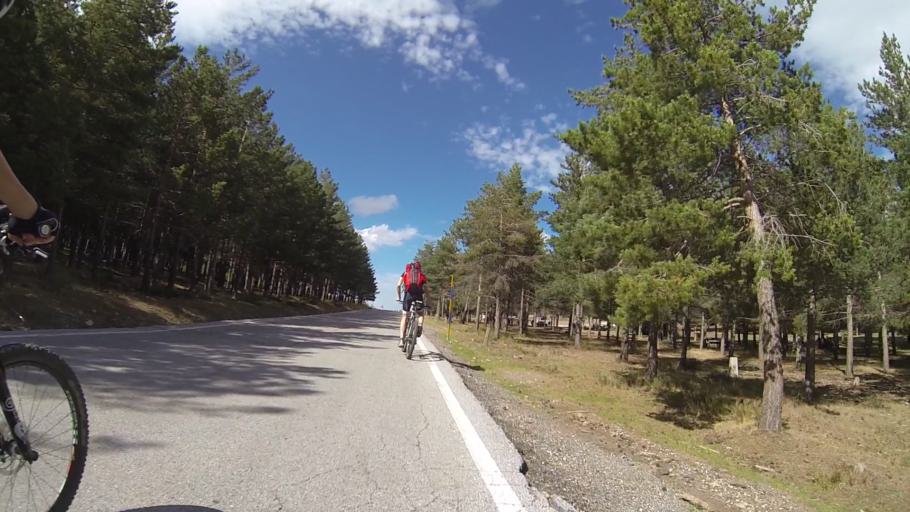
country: ES
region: Andalusia
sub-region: Provincia de Granada
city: Ferreira
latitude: 37.1125
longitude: -3.0295
